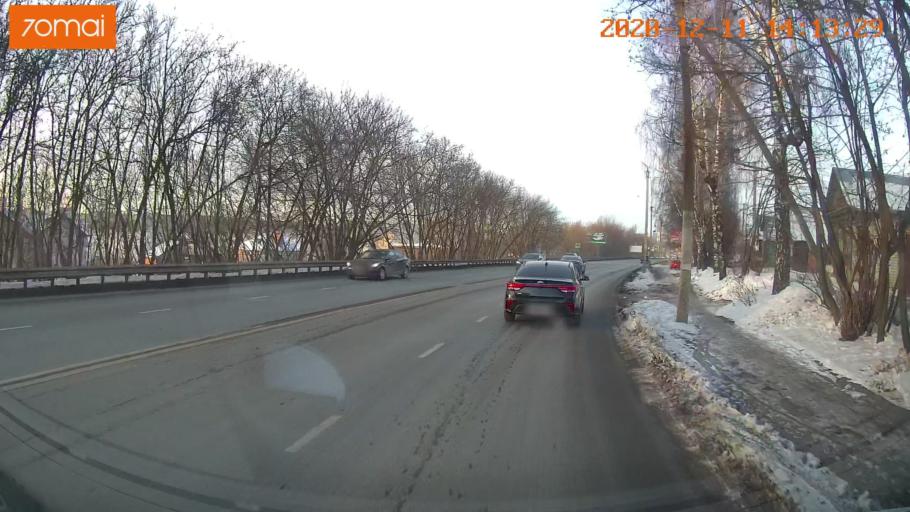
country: RU
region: Kostroma
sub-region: Kostromskoy Rayon
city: Kostroma
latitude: 57.7459
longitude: 40.9581
